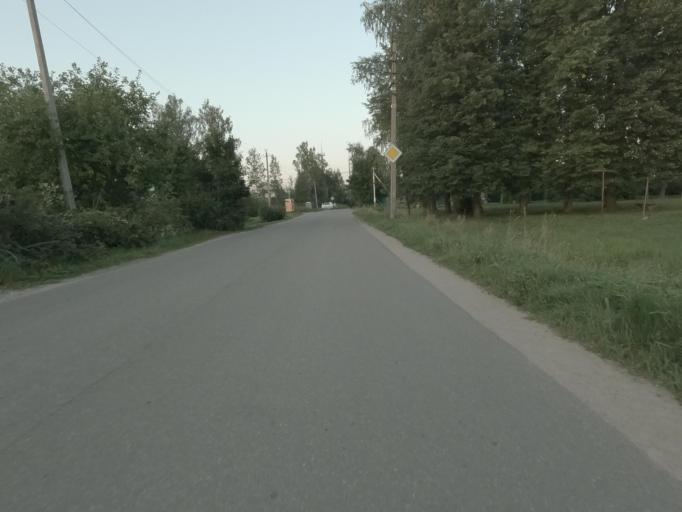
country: RU
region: Leningrad
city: Mga
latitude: 59.7605
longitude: 31.0605
